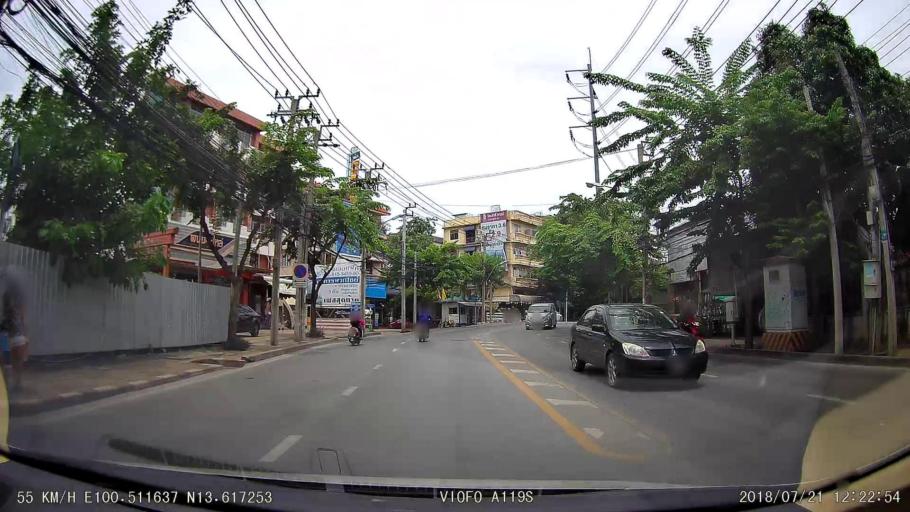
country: TH
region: Bangkok
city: Thung Khru
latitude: 13.6170
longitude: 100.5117
